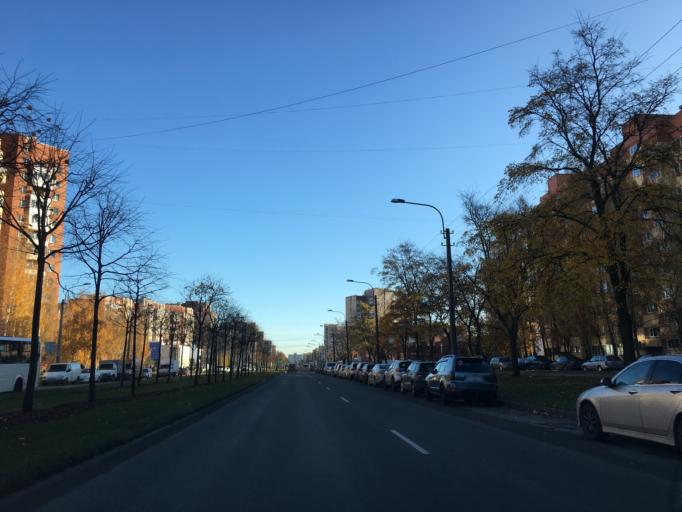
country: RU
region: St.-Petersburg
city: Uritsk
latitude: 59.8545
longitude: 30.1896
